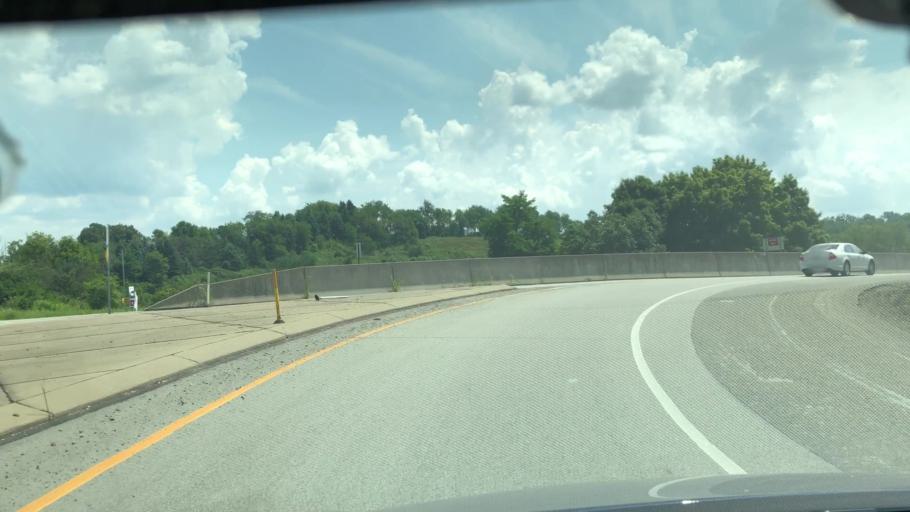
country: US
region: Pennsylvania
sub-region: Armstrong County
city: Freeport
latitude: 40.6917
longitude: -79.7120
